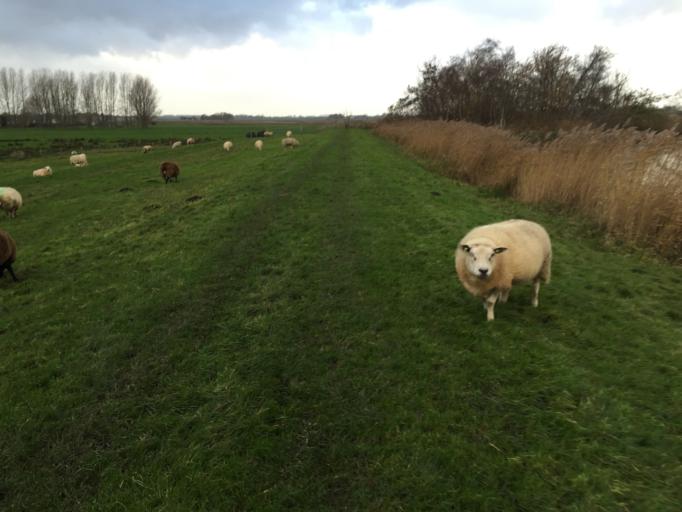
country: NL
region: North Holland
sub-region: Gemeente Ouder-Amstel
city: Ouderkerk aan de Amstel
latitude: 52.2450
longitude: 4.9226
